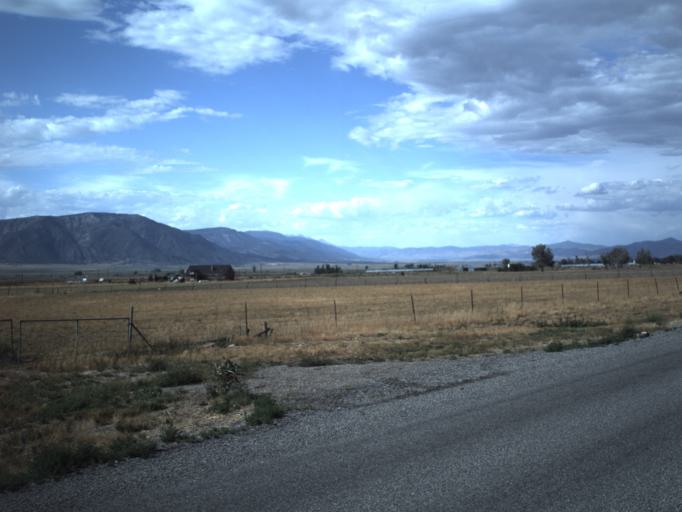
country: US
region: Utah
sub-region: Sanpete County
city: Ephraim
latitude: 39.3335
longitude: -111.5983
